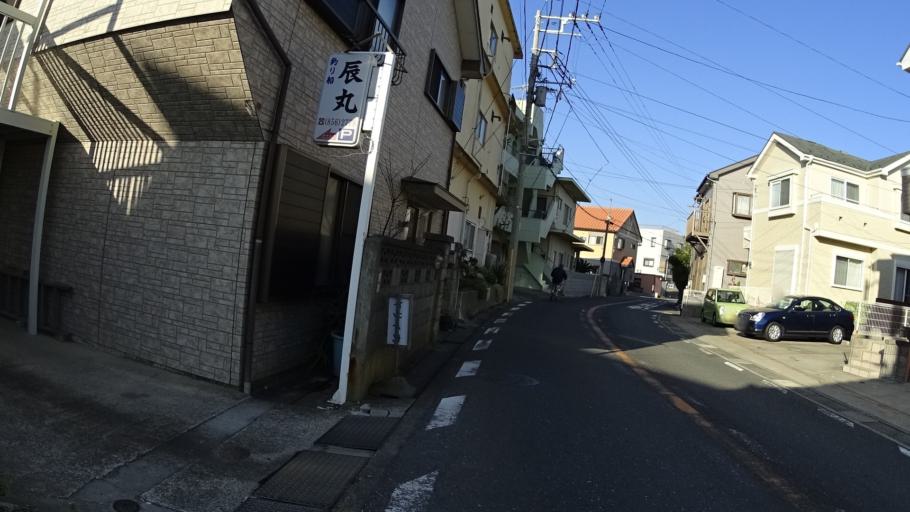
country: JP
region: Kanagawa
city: Miura
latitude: 35.2025
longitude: 139.6047
